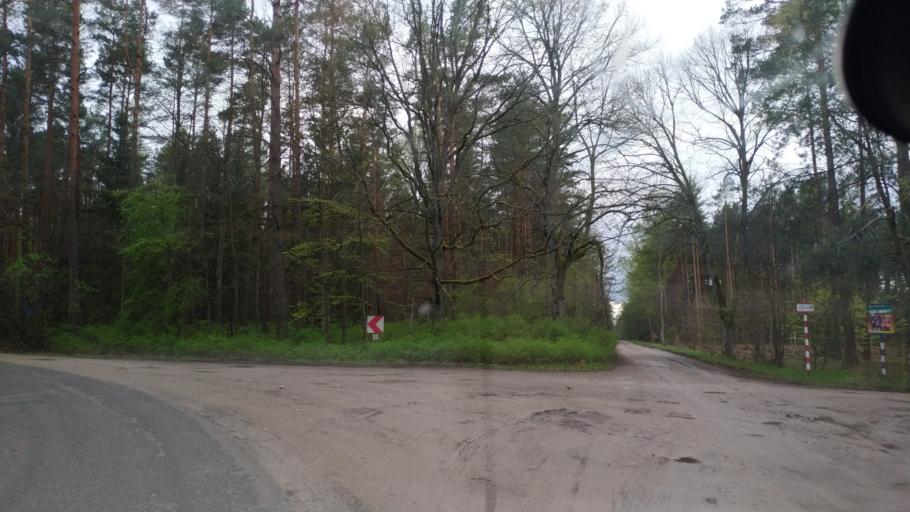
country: PL
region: Pomeranian Voivodeship
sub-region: Powiat starogardzki
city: Osiek
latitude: 53.6748
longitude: 18.4758
